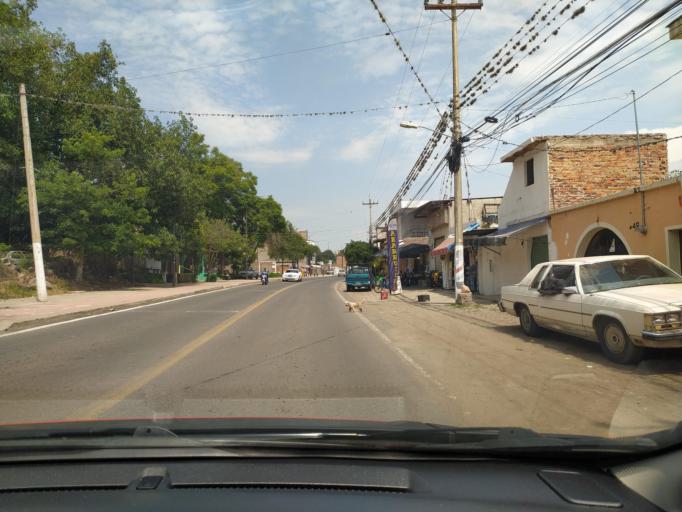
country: MX
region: Jalisco
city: San Juan Cosala
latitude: 20.2879
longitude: -103.3394
